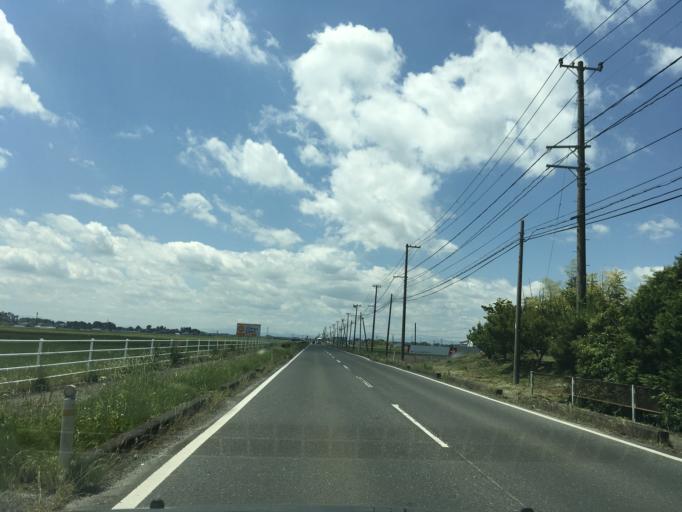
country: JP
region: Miyagi
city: Wakuya
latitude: 38.6775
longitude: 141.2394
